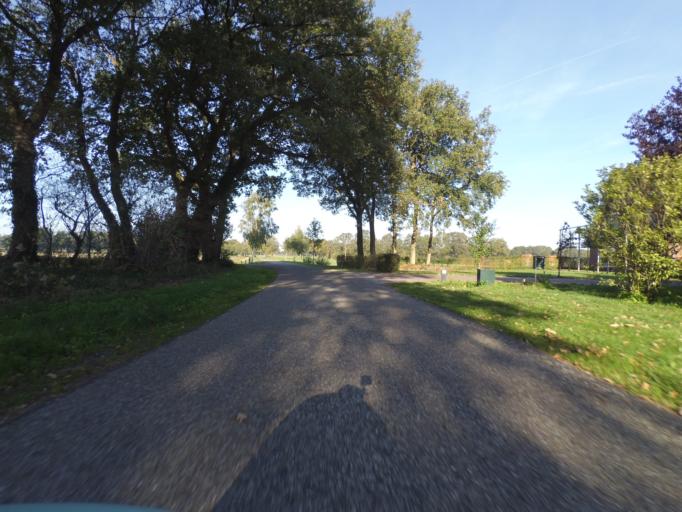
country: NL
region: Gelderland
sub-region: Berkelland
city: Eibergen
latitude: 52.0835
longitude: 6.6189
